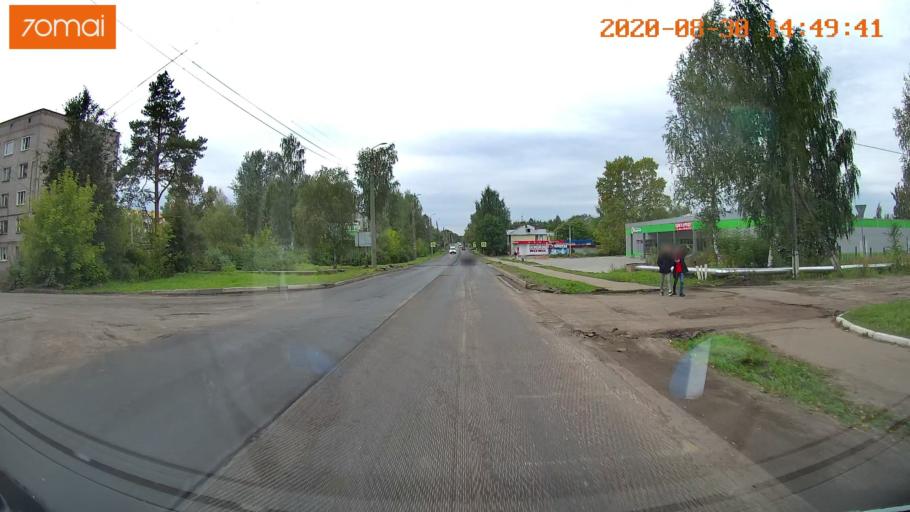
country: RU
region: Ivanovo
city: Kineshma
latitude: 57.4320
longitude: 42.1048
